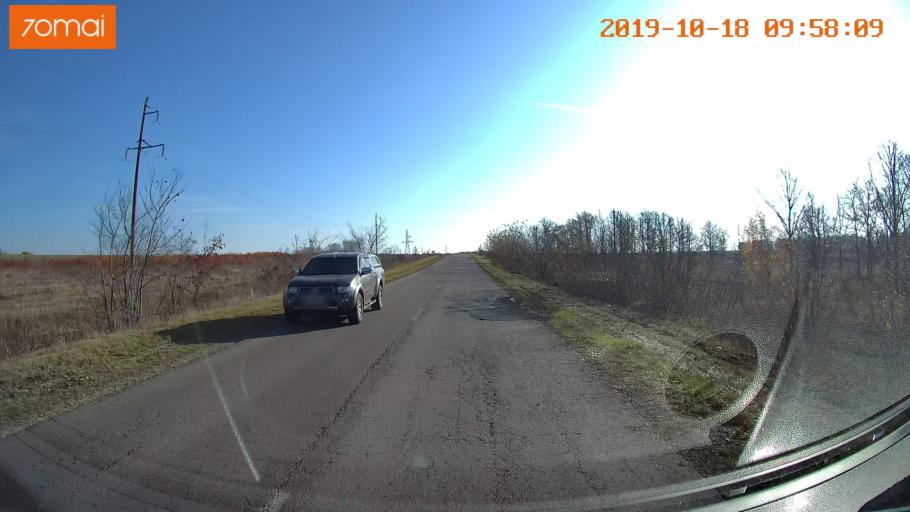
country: RU
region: Tula
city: Kurkino
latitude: 53.3754
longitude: 38.4337
